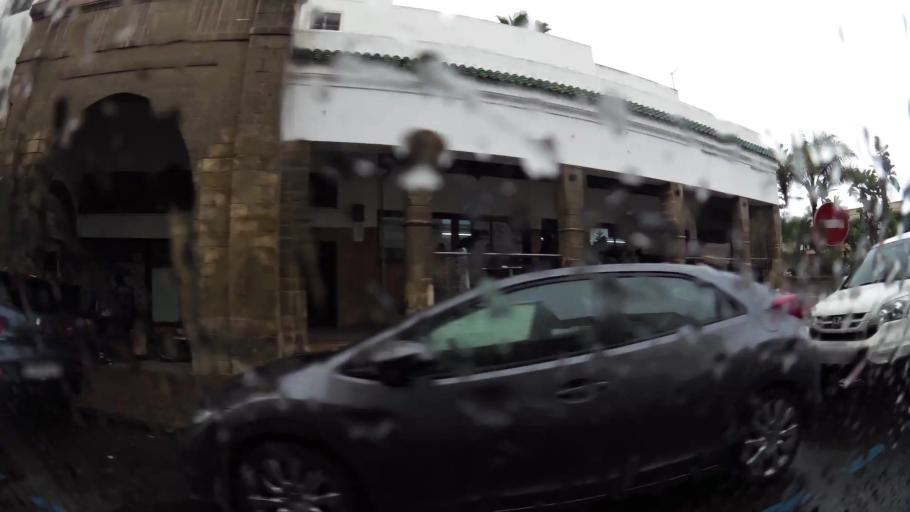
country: MA
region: Grand Casablanca
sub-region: Casablanca
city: Casablanca
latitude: 33.5788
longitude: -7.6060
